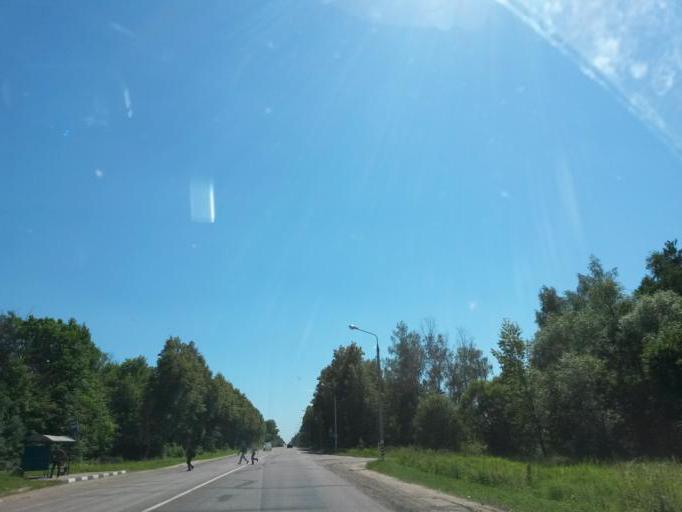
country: RU
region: Moskovskaya
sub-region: Chekhovskiy Rayon
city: Chekhov
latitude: 55.0813
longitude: 37.4400
